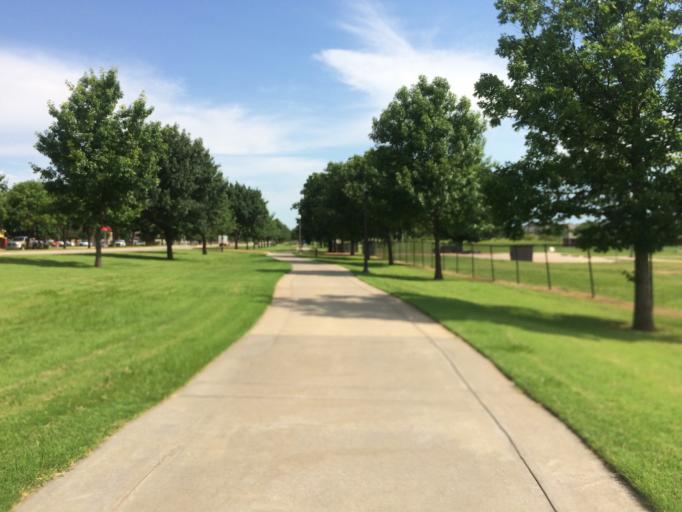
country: US
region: Oklahoma
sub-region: Cleveland County
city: Norman
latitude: 35.1873
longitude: -97.4498
